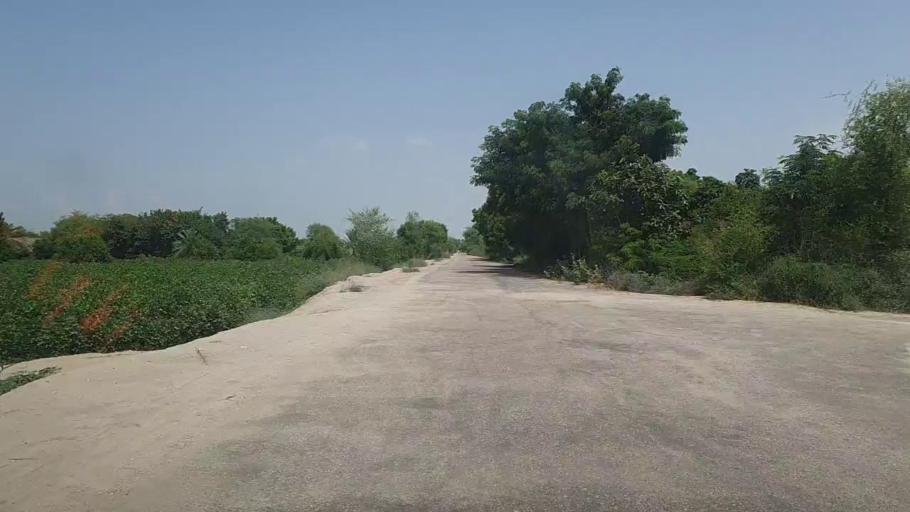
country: PK
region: Sindh
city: Pad Idan
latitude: 26.8430
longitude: 68.3407
